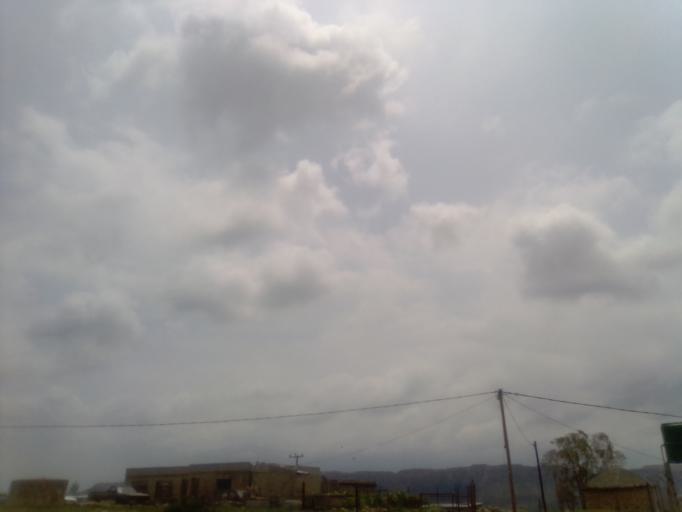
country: LS
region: Leribe
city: Leribe
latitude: -29.0373
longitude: 28.0194
